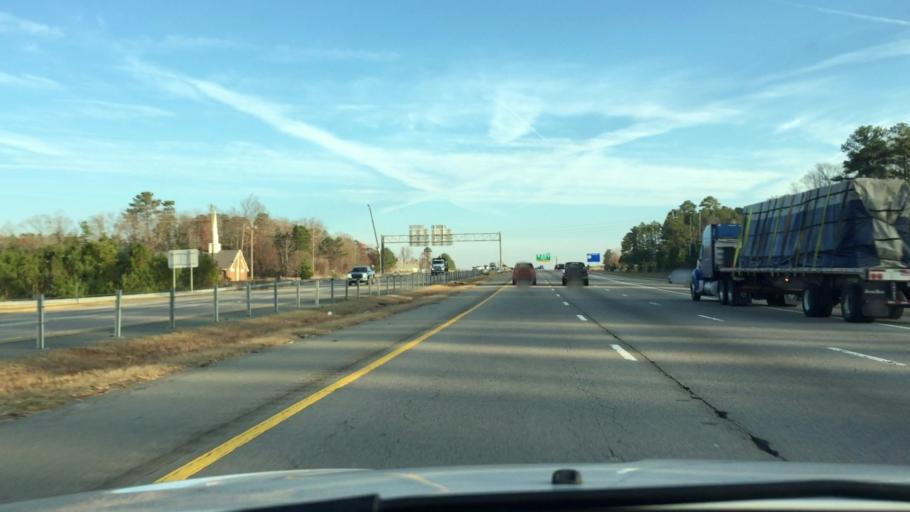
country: US
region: North Carolina
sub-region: Lee County
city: Sanford
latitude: 35.5142
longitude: -79.1869
